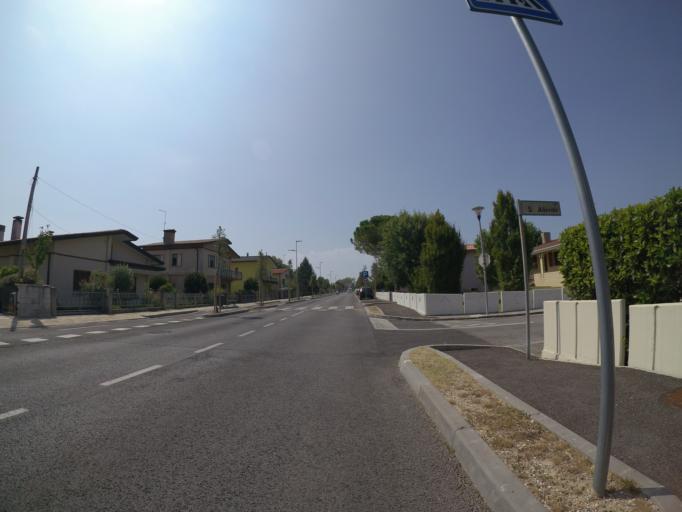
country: IT
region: Veneto
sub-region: Provincia di Venezia
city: Bibione
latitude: 45.6662
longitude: 13.0600
